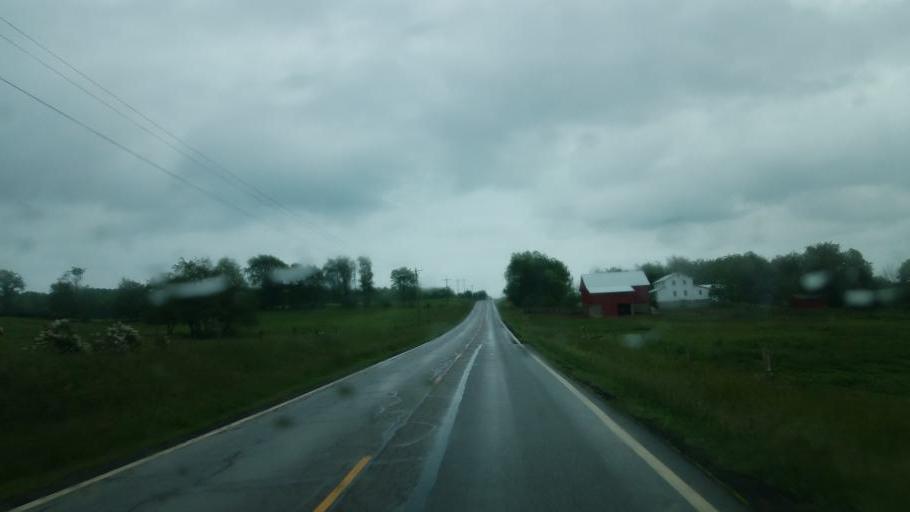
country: US
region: Ohio
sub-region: Knox County
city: Oak Hill
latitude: 40.3436
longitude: -82.2852
